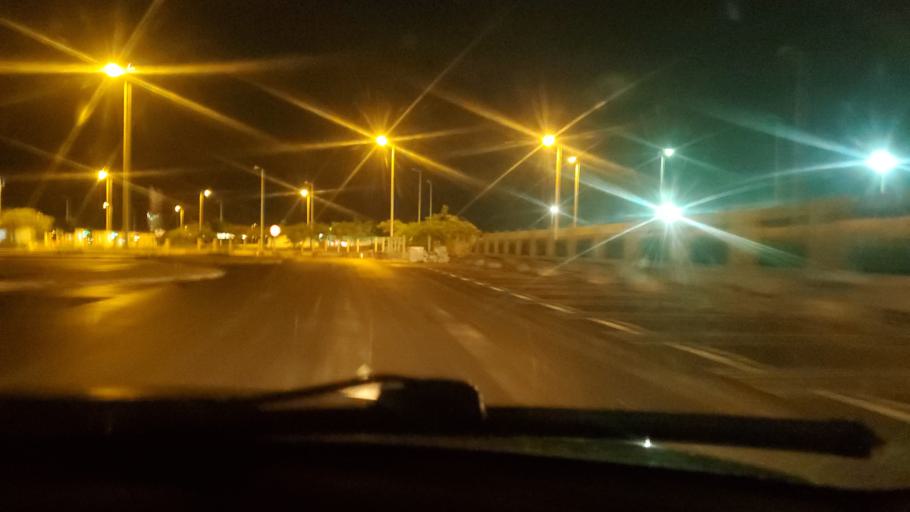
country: SN
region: Thies
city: Pout
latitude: 14.6695
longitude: -17.0664
